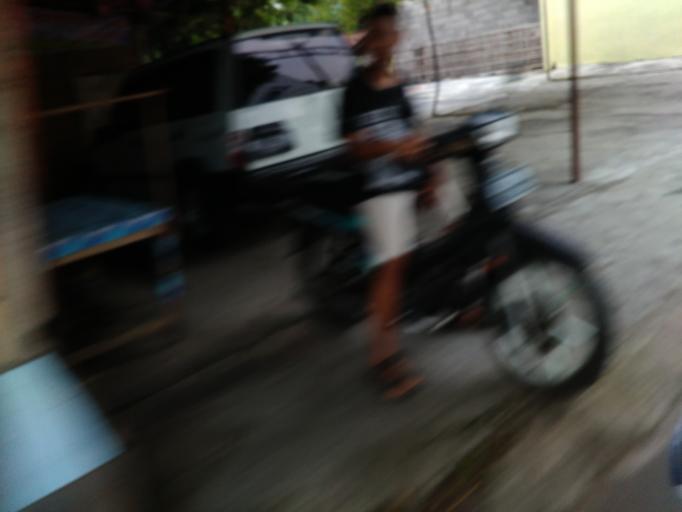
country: ID
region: Central Java
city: Boyolali
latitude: -7.5445
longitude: 110.6046
